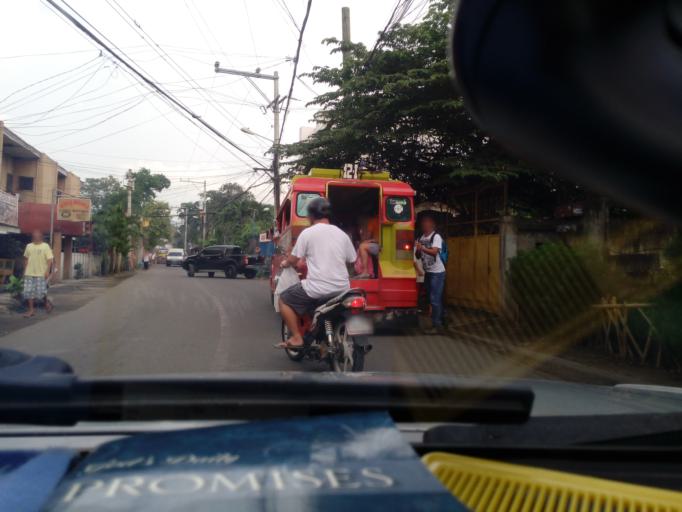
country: PH
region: Central Visayas
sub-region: Cebu City
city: Calero
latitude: 10.2974
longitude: 123.8779
